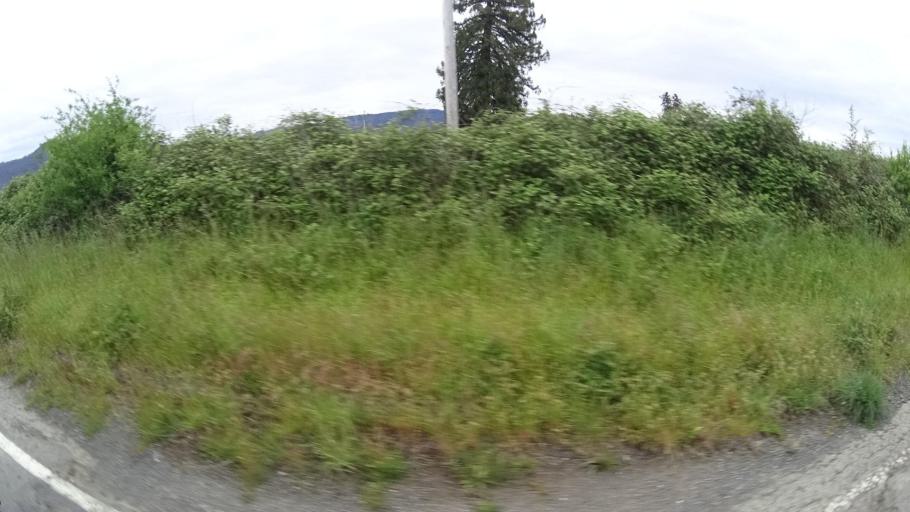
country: US
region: California
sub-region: Humboldt County
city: Blue Lake
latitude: 40.8621
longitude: -123.9957
